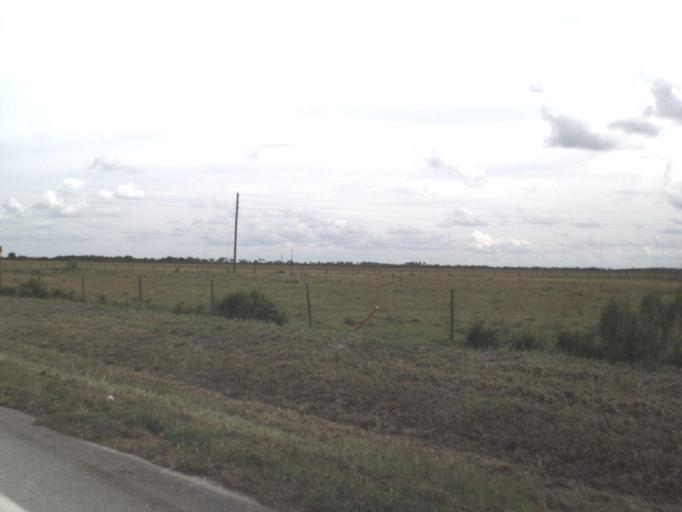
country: US
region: Florida
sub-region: Okeechobee County
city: Taylor Creek
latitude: 27.2789
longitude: -80.7137
